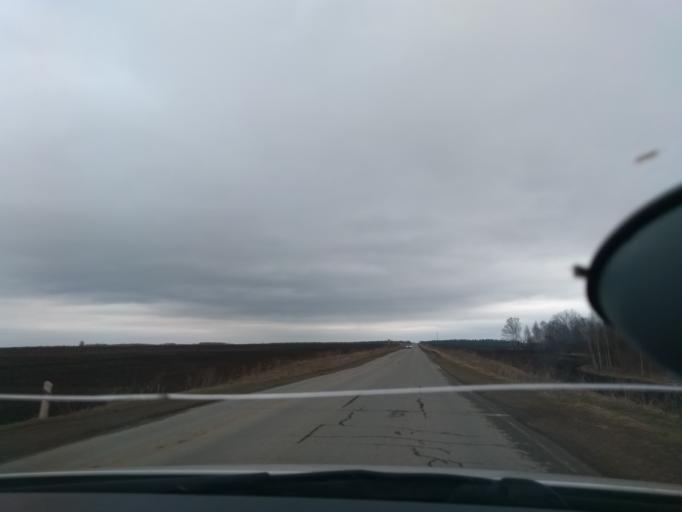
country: RU
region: Perm
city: Kungur
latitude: 57.3804
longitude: 56.8501
